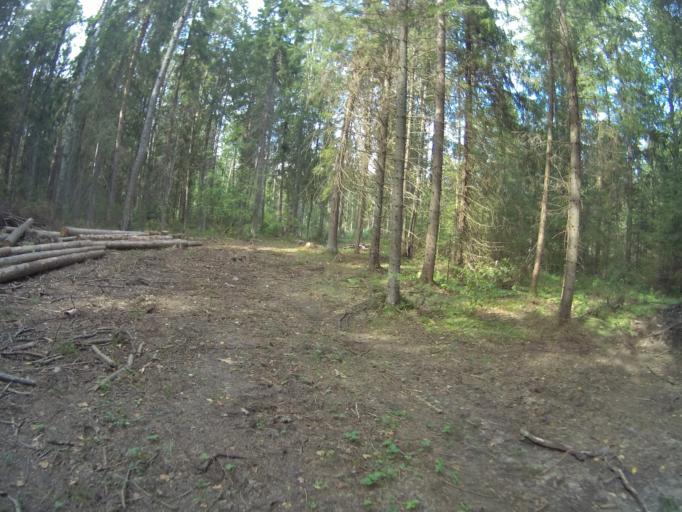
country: RU
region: Vladimir
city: Orgtrud
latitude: 56.1187
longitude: 40.5852
